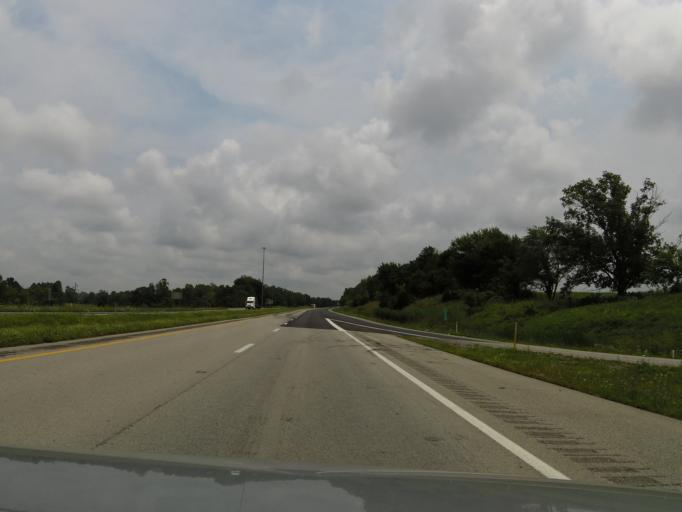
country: US
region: Kentucky
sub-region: Grayson County
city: Leitchfield
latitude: 37.4897
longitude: -86.2072
